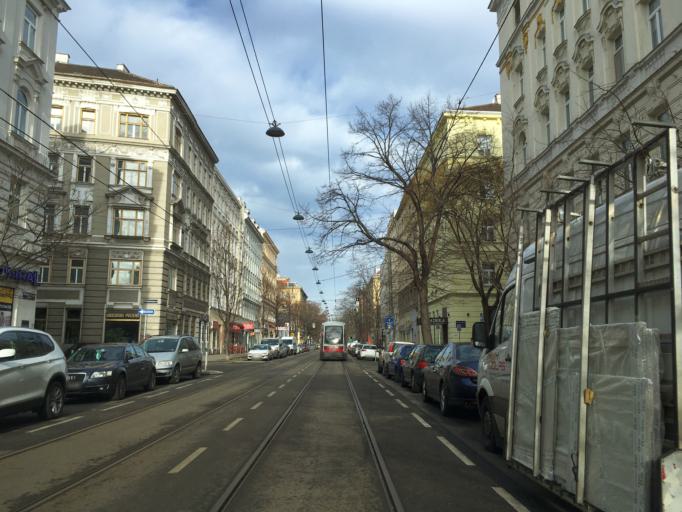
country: AT
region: Vienna
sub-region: Wien Stadt
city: Vienna
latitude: 48.2324
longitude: 16.3662
